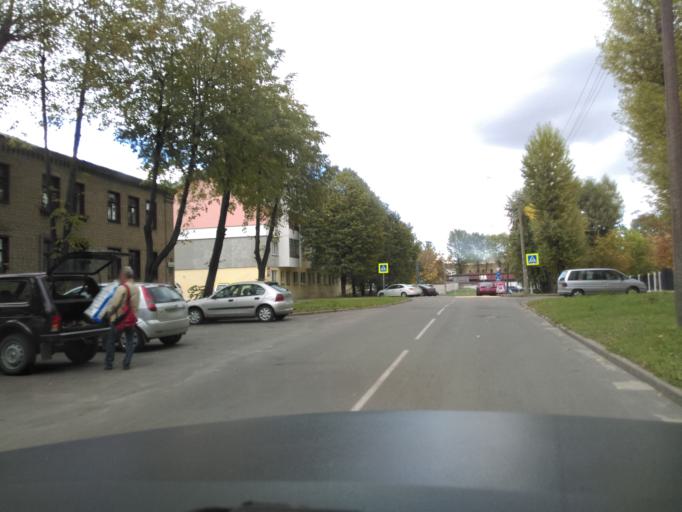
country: BY
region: Minsk
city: Minsk
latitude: 53.9087
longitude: 27.6297
